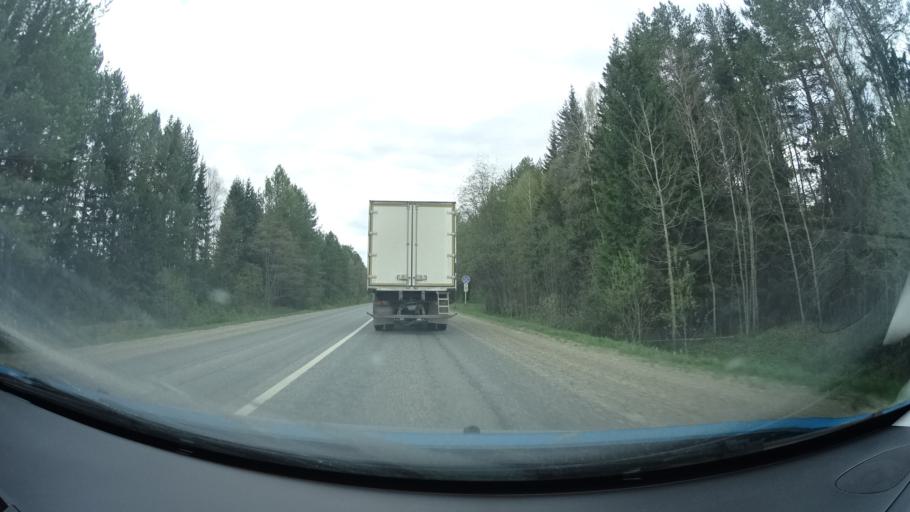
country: RU
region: Perm
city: Yugo-Kamskiy
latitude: 57.5672
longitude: 55.6806
